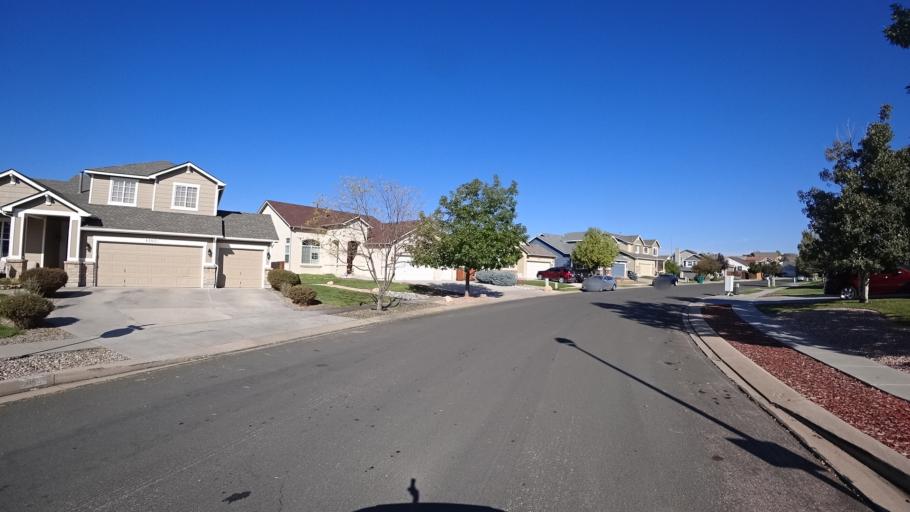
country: US
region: Colorado
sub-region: El Paso County
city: Cimarron Hills
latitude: 38.8902
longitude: -104.6954
